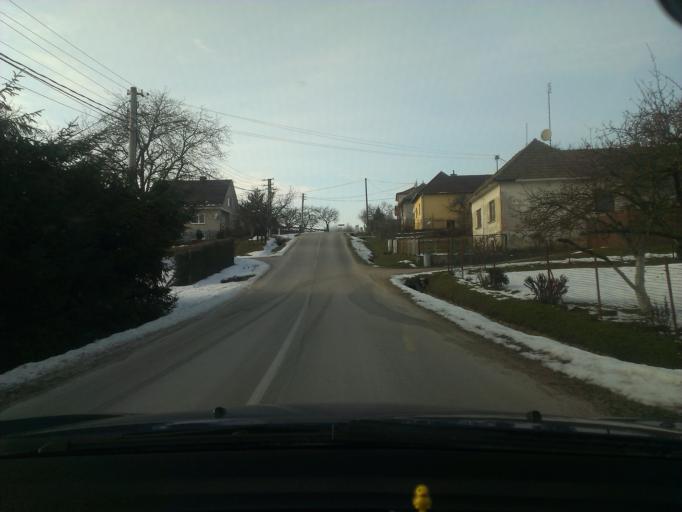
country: SK
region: Nitriansky
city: Stara Tura
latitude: 48.7357
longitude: 17.6565
